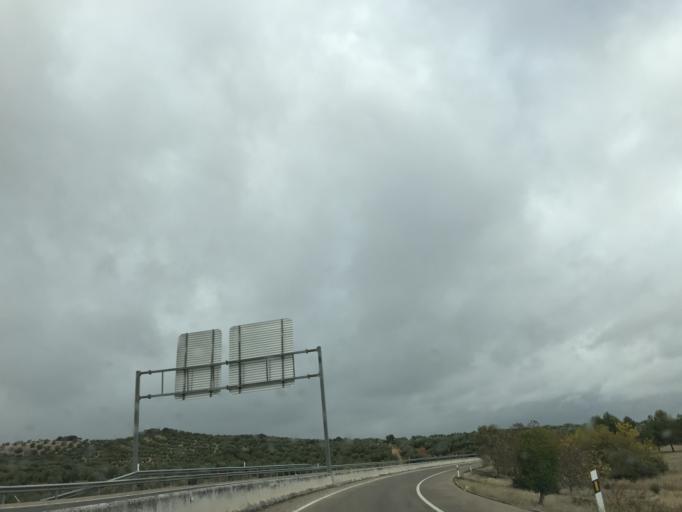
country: ES
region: Andalusia
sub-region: Provincia de Jaen
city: Bailen
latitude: 38.1214
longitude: -3.7614
